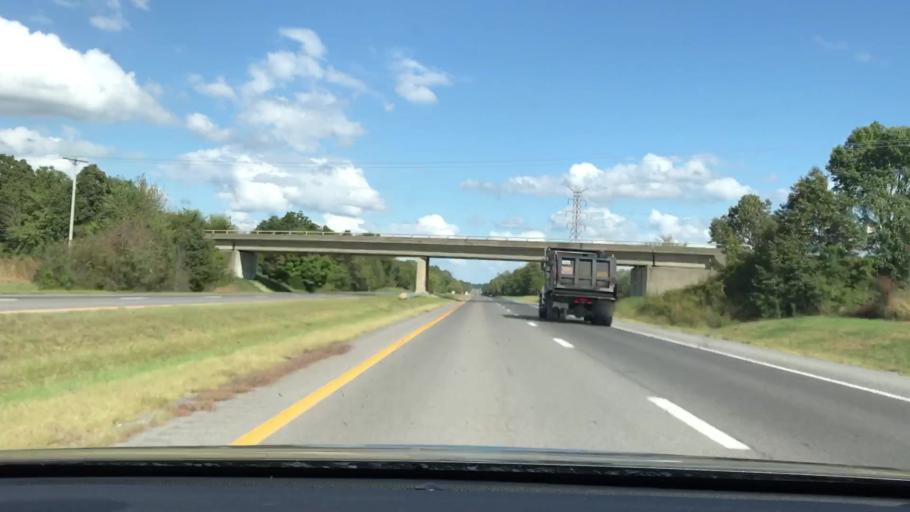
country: US
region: Kentucky
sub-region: Marshall County
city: Benton
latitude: 36.8271
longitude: -88.4581
